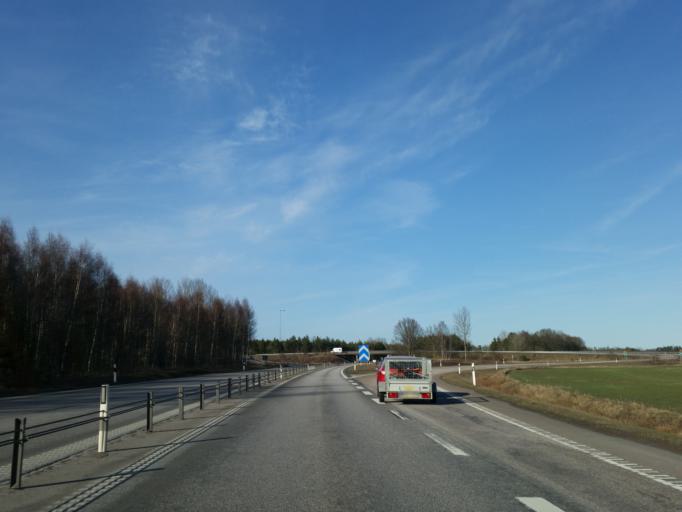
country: SE
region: Kalmar
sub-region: Kalmar Kommun
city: Lindsdal
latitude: 56.7549
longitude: 16.3068
